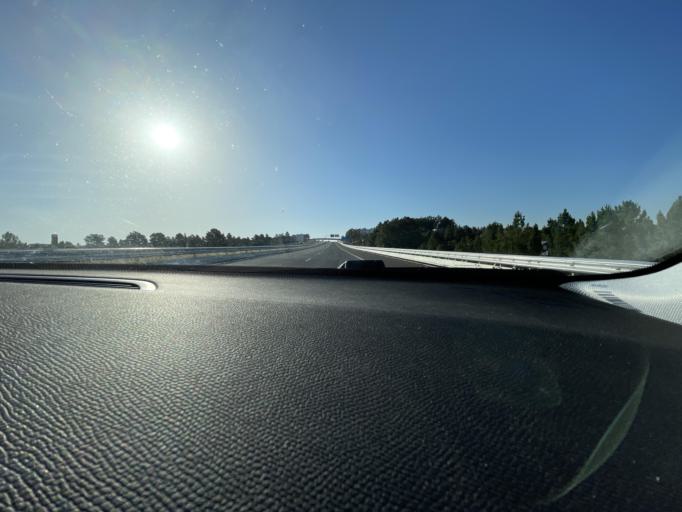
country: ES
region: Castille and Leon
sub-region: Provincia de Salamanca
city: Fuentes de Onoro
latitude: 40.6165
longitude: -6.8292
